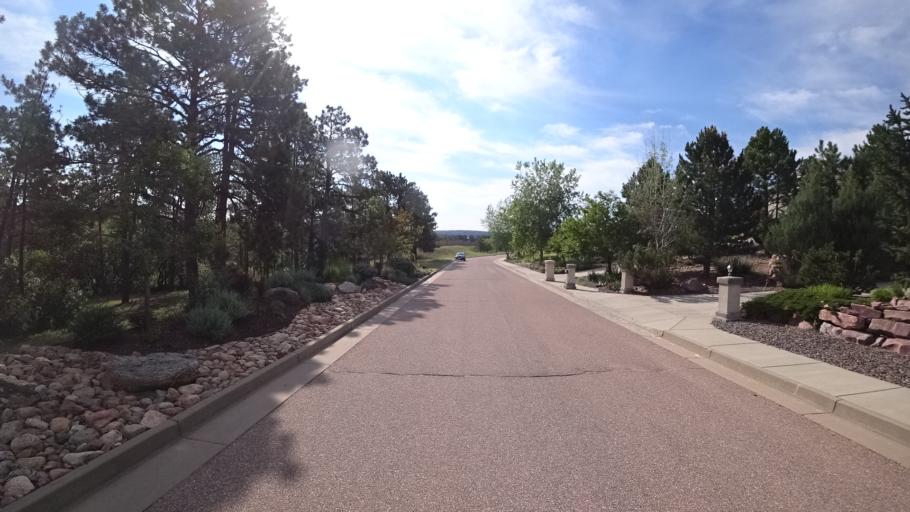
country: US
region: Colorado
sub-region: El Paso County
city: Air Force Academy
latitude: 38.9439
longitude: -104.8269
